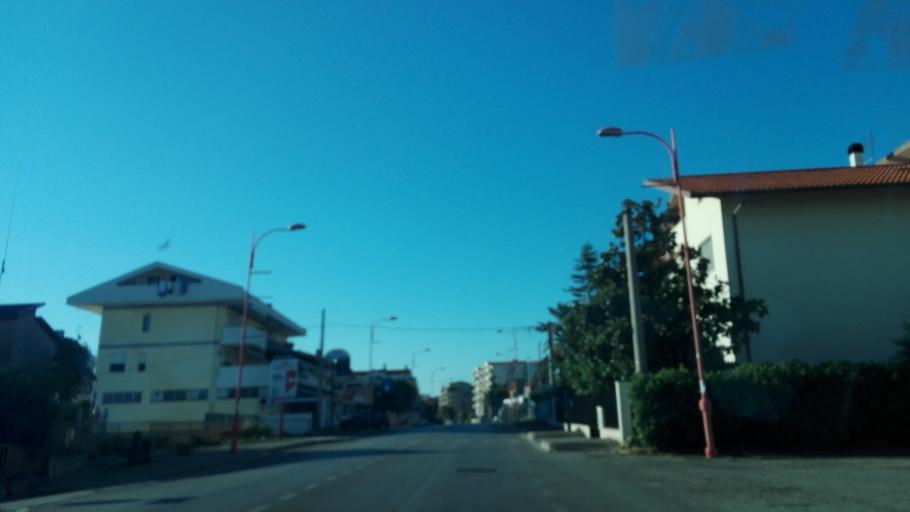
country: IT
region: Abruzzo
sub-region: Provincia di Pescara
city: Montesilvano Marina
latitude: 42.4996
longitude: 14.1674
